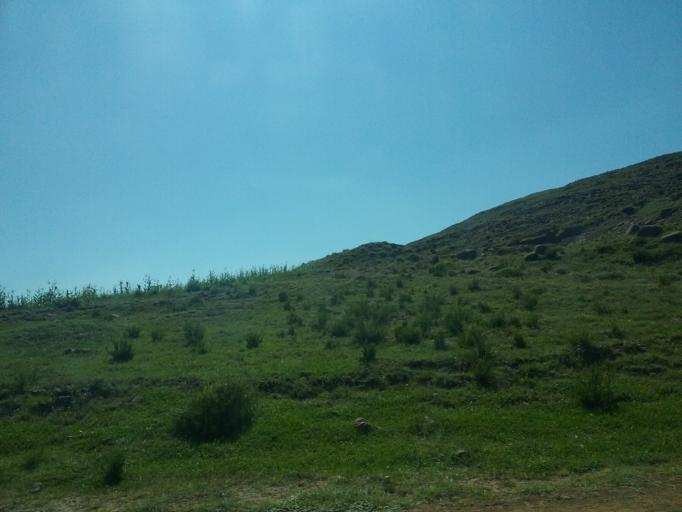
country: LS
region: Berea
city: Teyateyaneng
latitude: -29.2158
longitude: 27.8483
